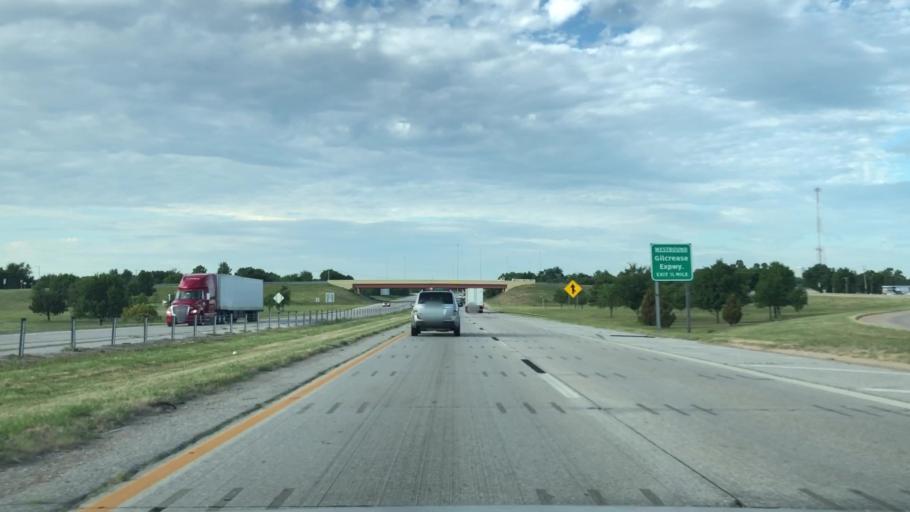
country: US
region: Oklahoma
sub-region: Tulsa County
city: Turley
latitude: 36.2092
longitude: -95.9461
